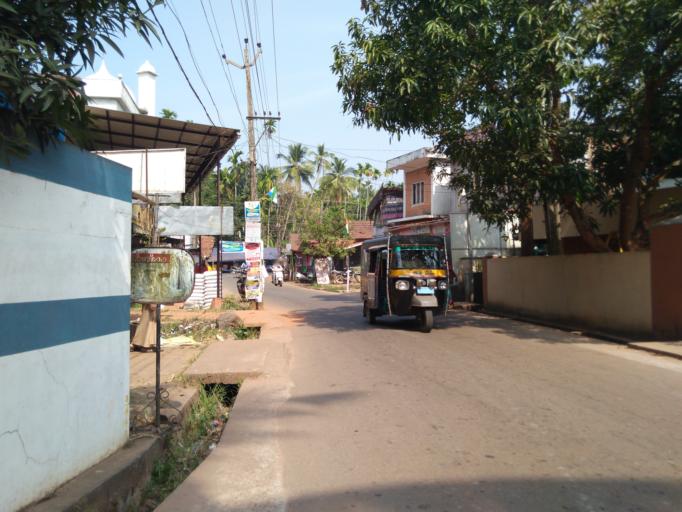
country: IN
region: Kerala
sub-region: Kozhikode
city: Kunnamangalam
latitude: 11.2963
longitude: 75.8351
